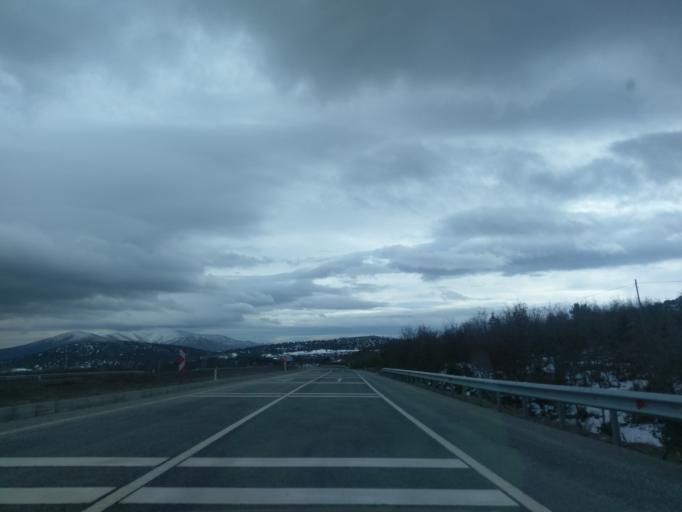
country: TR
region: Kuetahya
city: Aslanapa
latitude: 39.2756
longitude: 29.9167
